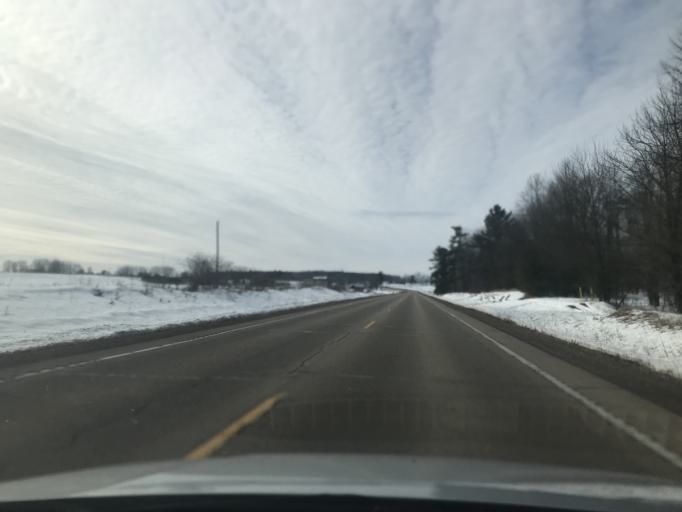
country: US
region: Wisconsin
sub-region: Oconto County
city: Gillett
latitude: 44.8830
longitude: -88.3397
